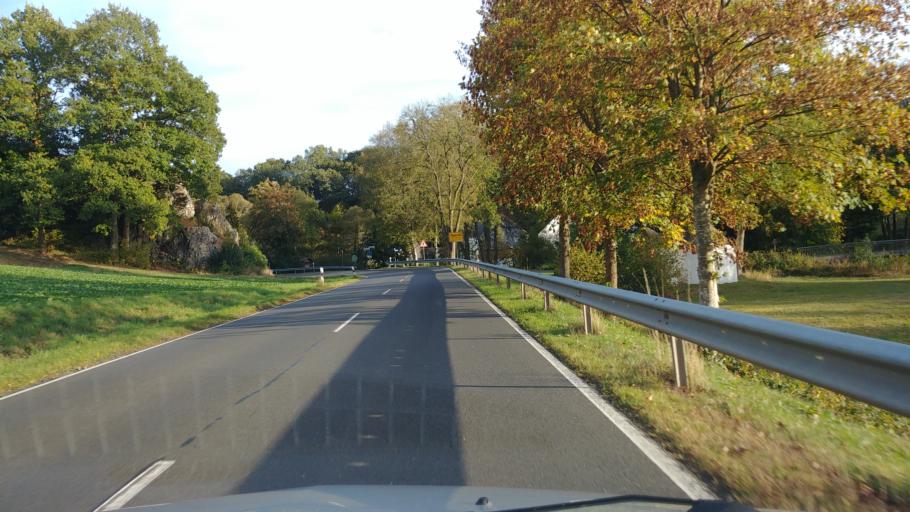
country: DE
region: Rheinland-Pfalz
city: Morbach
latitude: 49.8178
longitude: 7.0929
